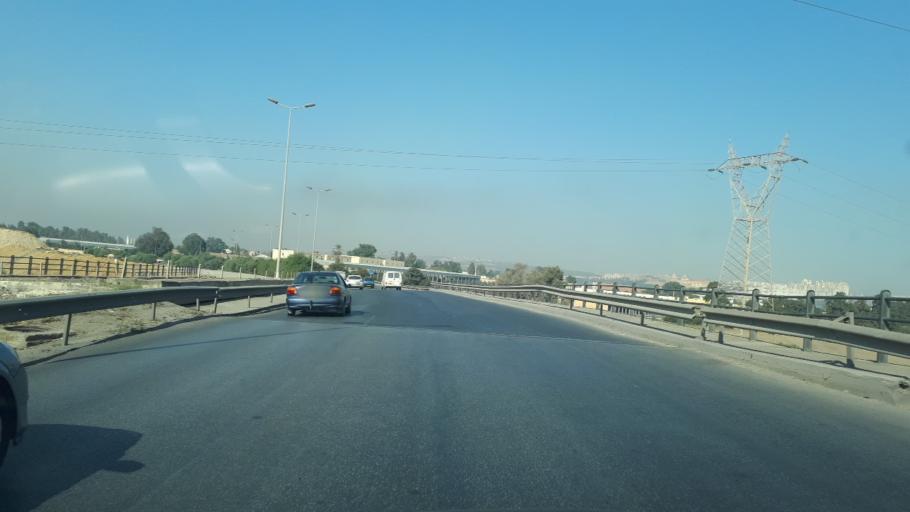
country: DZ
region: Tipaza
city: Baraki
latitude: 36.6831
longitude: 3.0981
